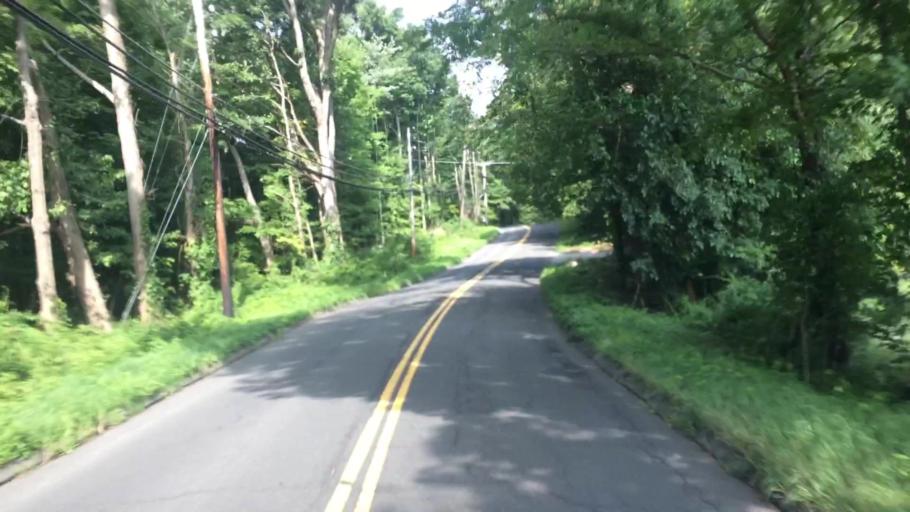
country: US
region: Connecticut
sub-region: Fairfield County
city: Danbury
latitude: 41.4023
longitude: -73.4738
